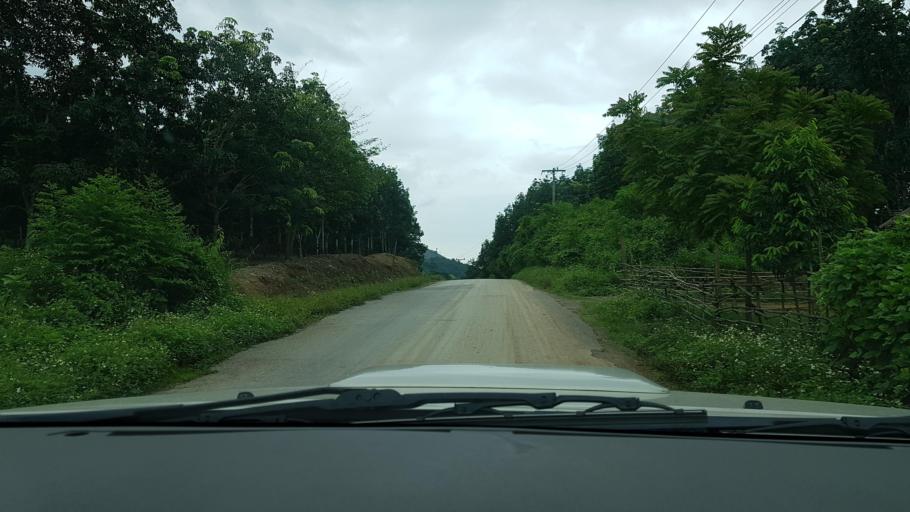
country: LA
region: Loungnamtha
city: Muang Nale
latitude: 20.2336
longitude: 101.5651
